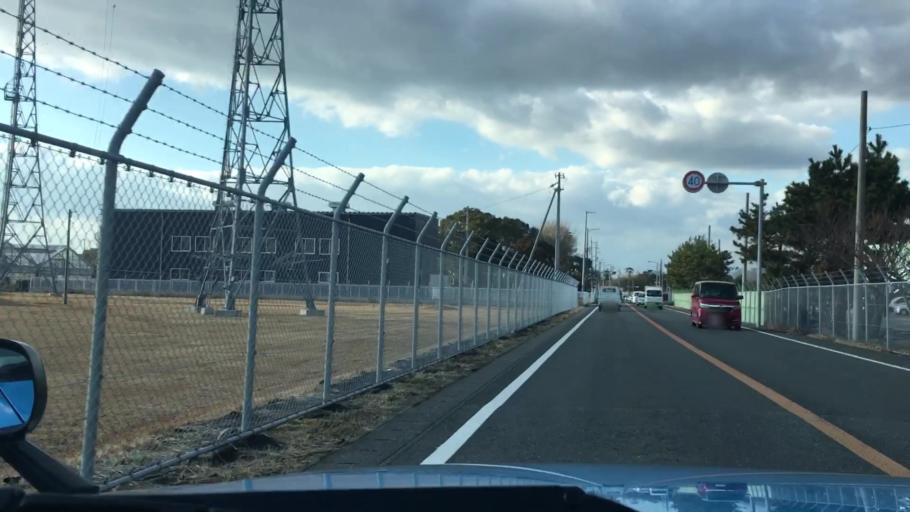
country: JP
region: Shizuoka
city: Hamamatsu
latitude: 34.7458
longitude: 137.6876
